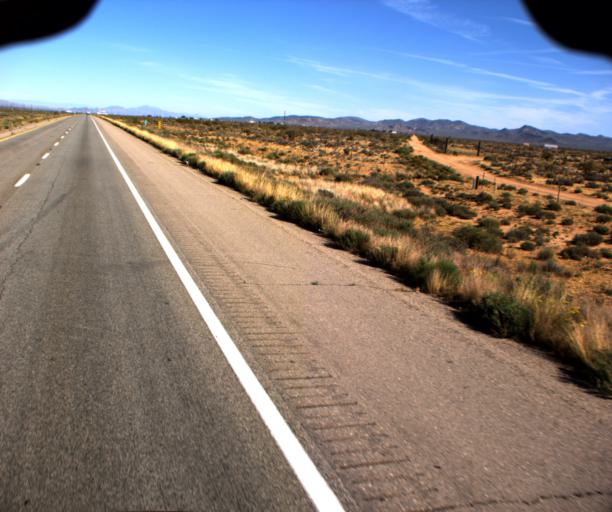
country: US
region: Arizona
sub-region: Mohave County
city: Dolan Springs
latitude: 35.5190
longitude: -114.3448
